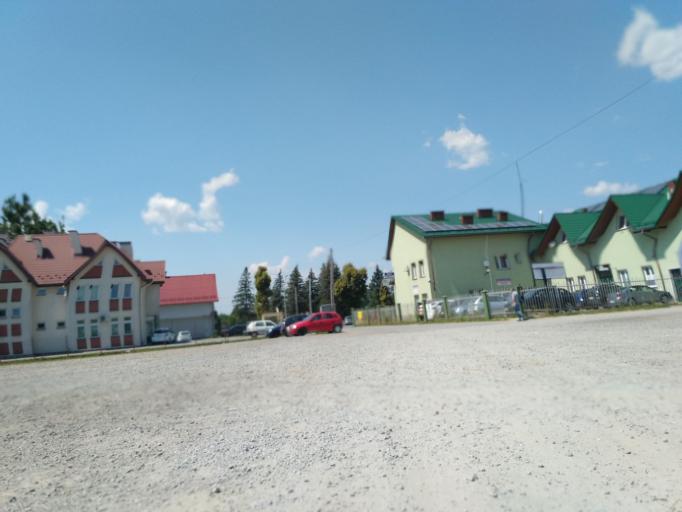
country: PL
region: Subcarpathian Voivodeship
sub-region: Powiat brzozowski
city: Brzozow
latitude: 49.7008
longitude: 22.0211
